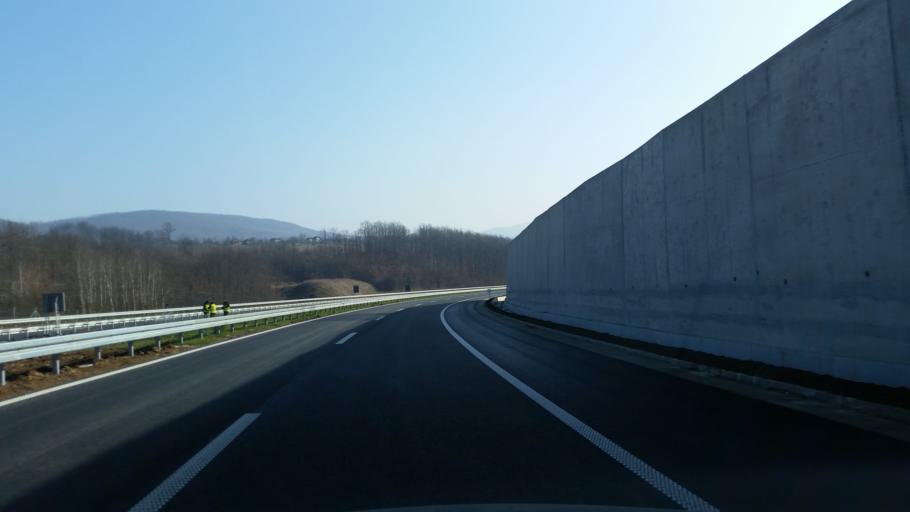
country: RS
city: Prislonica
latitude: 44.0121
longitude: 20.3809
